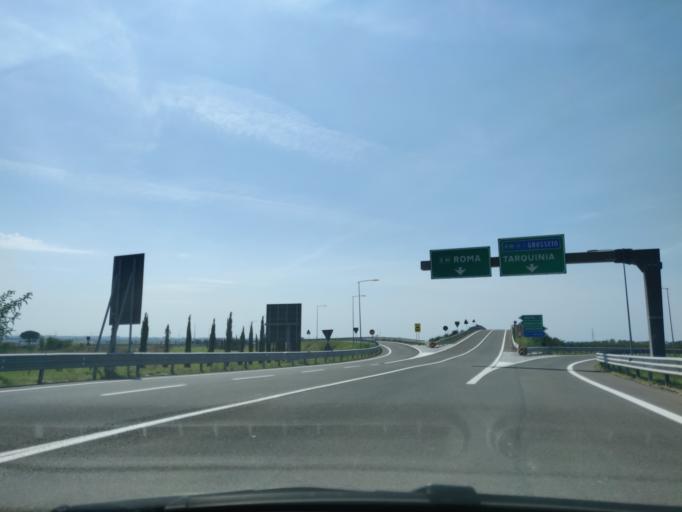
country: IT
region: Latium
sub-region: Provincia di Viterbo
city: Tarquinia
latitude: 42.2134
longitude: 11.7817
